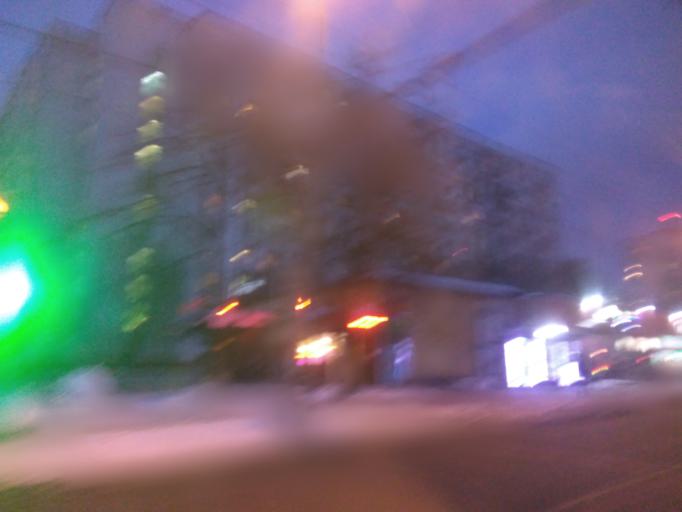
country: RU
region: Moscow
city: Lyublino
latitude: 55.6728
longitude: 37.7465
